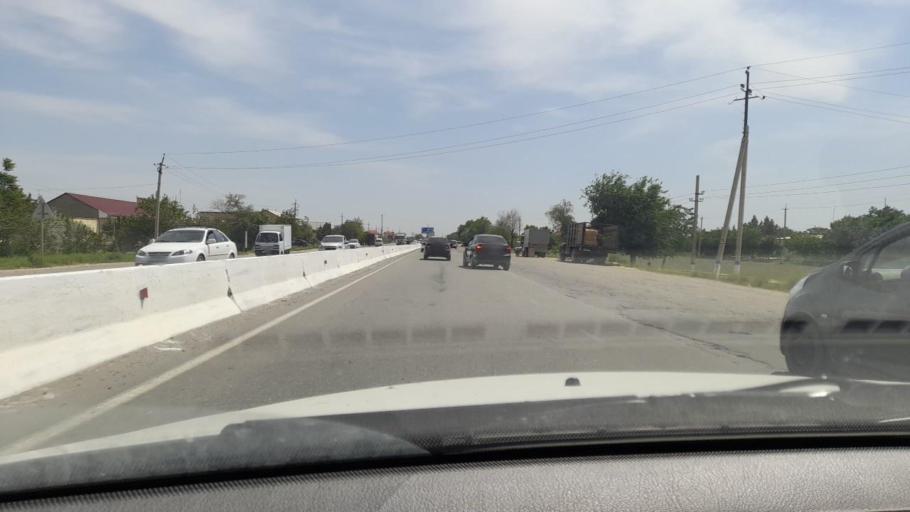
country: UZ
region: Bukhara
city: Ghijduwon
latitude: 40.0879
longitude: 64.6675
